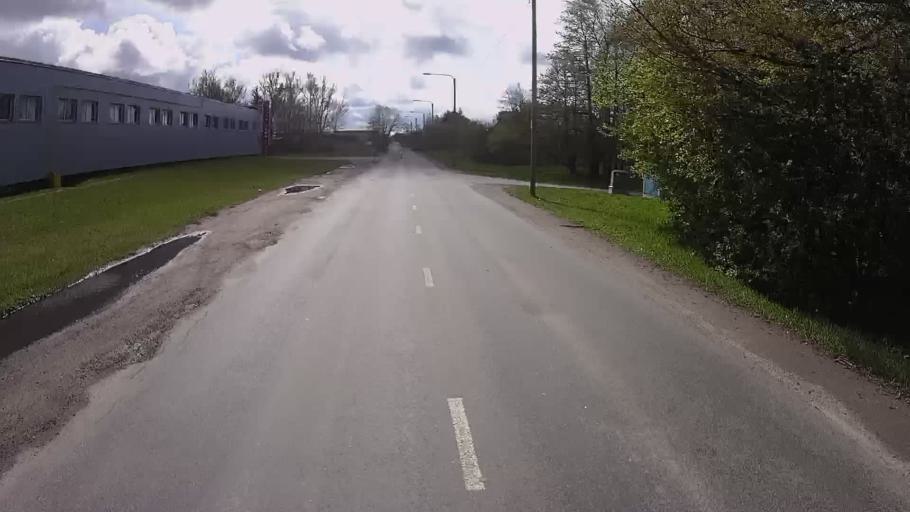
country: EE
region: Harju
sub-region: Tallinna linn
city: Tallinn
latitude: 59.4242
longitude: 24.6879
